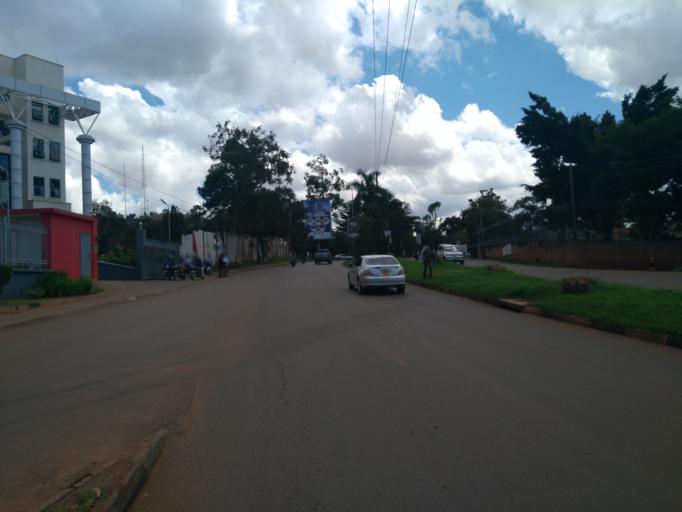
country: UG
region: Central Region
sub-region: Kampala District
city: Kampala
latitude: 0.3281
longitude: 32.6036
